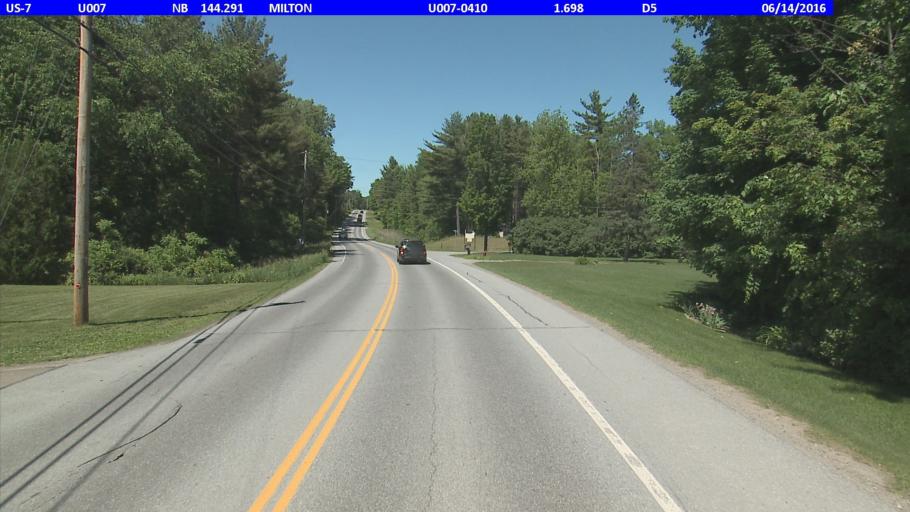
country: US
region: Vermont
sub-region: Chittenden County
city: Milton
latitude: 44.6175
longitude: -73.1497
